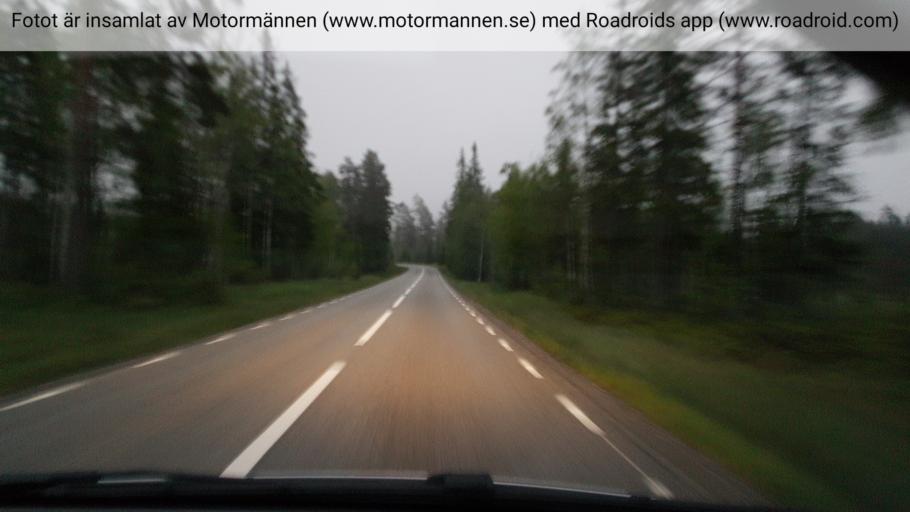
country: SE
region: OErebro
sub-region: Lindesbergs Kommun
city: Stora
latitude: 59.8917
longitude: 15.2491
